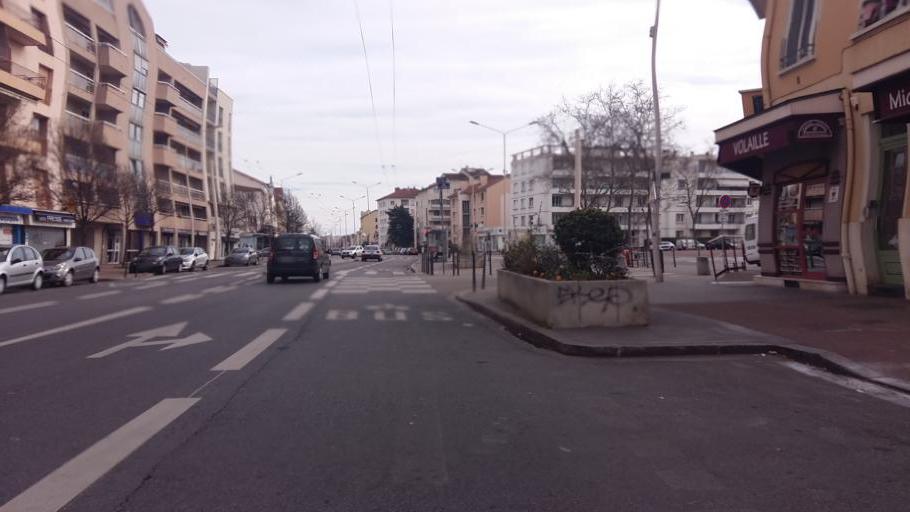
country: FR
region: Rhone-Alpes
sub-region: Departement du Rhone
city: Saint-Fons
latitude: 45.7282
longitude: 4.8774
